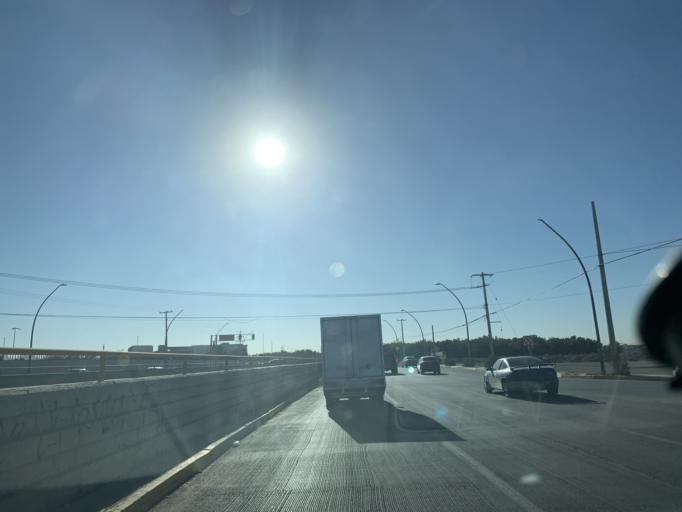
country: US
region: Texas
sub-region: El Paso County
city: Socorro
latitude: 31.6742
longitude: -106.3872
